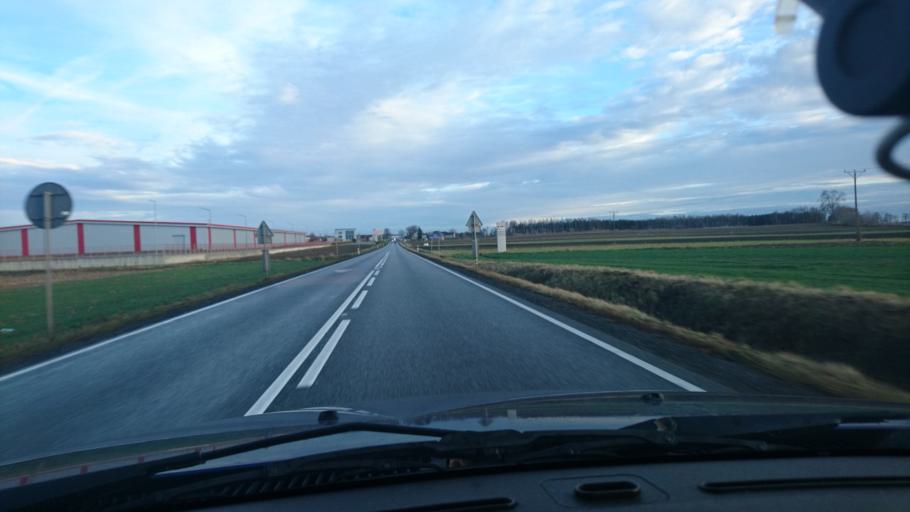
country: PL
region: Greater Poland Voivodeship
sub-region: Powiat kepinski
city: Slupia pod Kepnem
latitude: 51.2323
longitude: 18.0667
